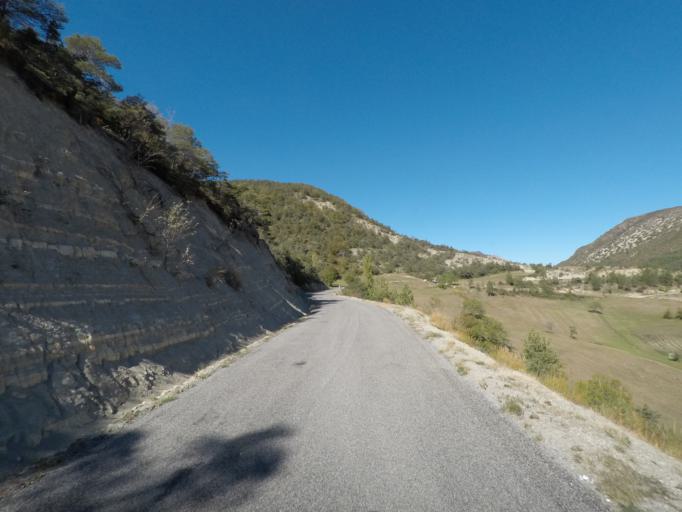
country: FR
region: Rhone-Alpes
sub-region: Departement de la Drome
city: Die
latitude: 44.5729
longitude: 5.3027
